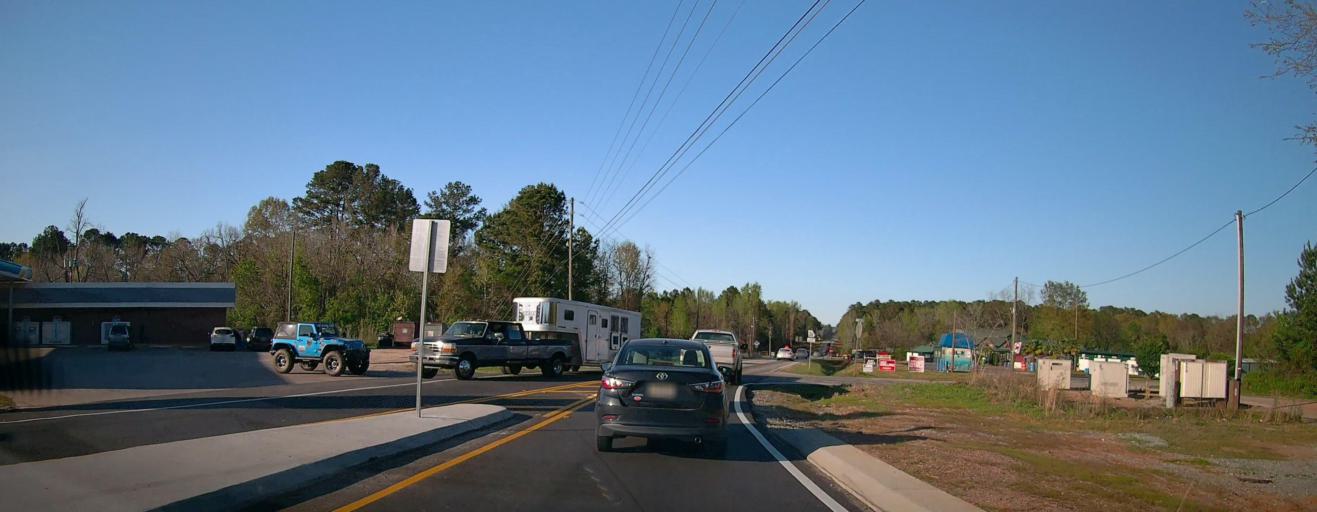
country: US
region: Georgia
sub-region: Butts County
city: Jackson
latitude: 33.3837
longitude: -83.9032
